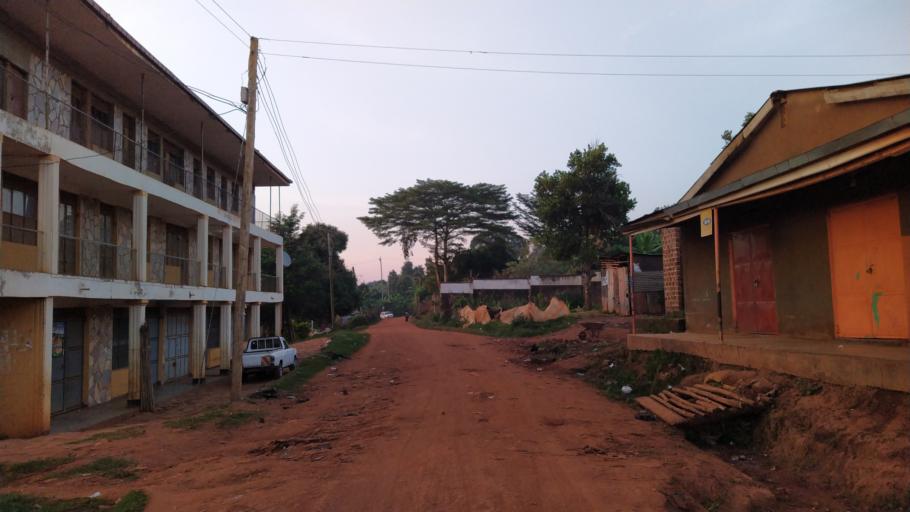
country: UG
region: Central Region
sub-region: Kampala District
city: Kampala
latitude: 0.2723
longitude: 32.5745
